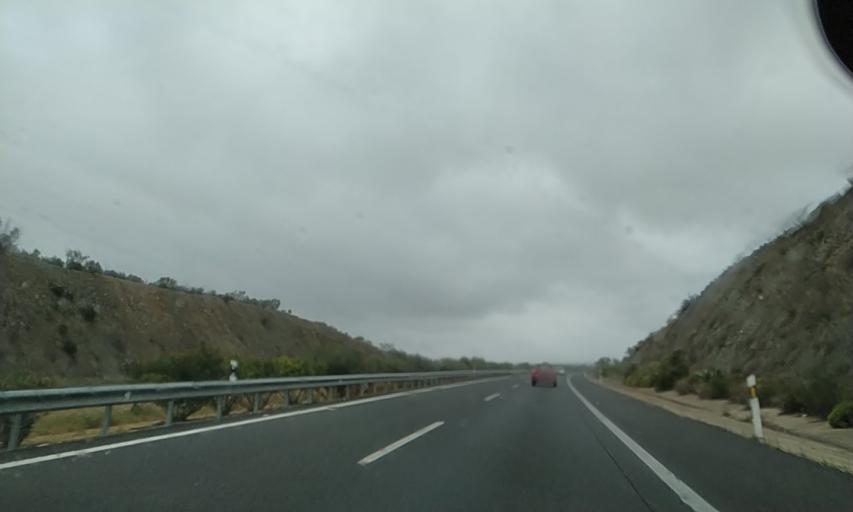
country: ES
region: Extremadura
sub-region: Provincia de Caceres
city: Canaveral
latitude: 39.7527
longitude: -6.4003
